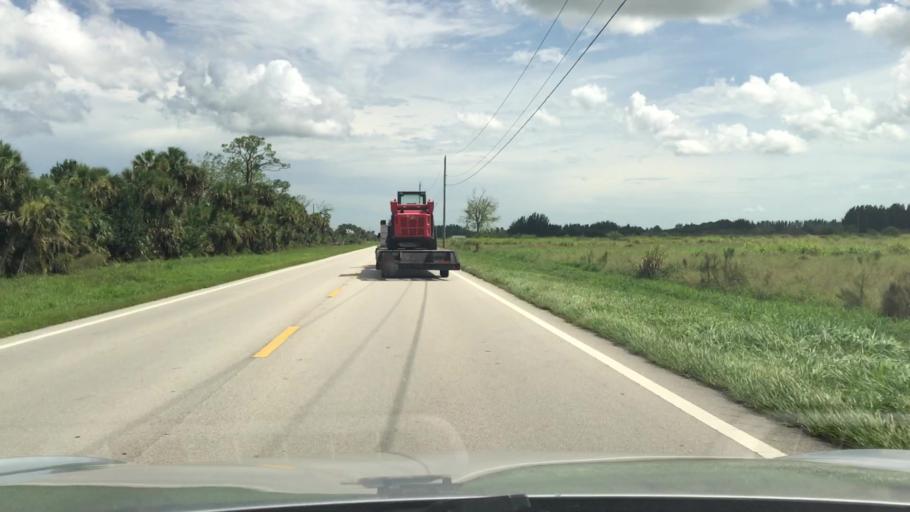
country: US
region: Florida
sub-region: Indian River County
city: Winter Beach
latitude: 27.7074
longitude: -80.4626
